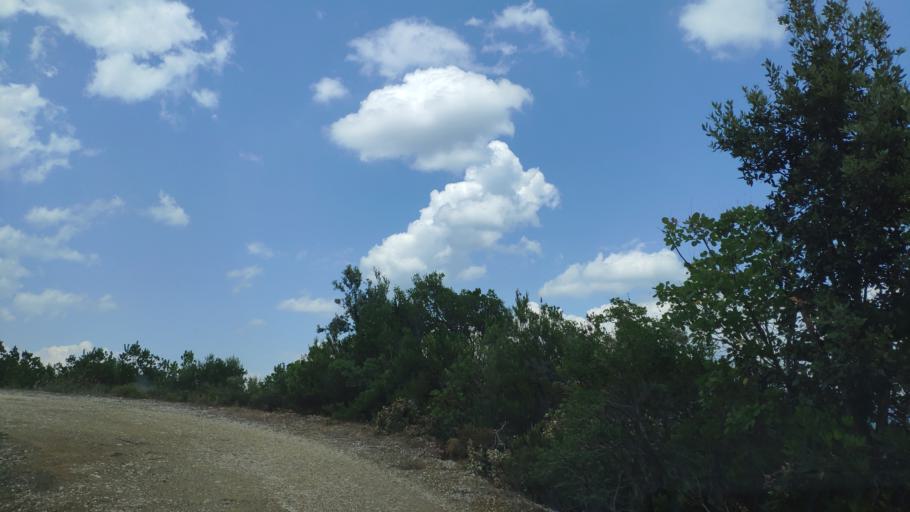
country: GR
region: Epirus
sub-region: Nomos Artas
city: Agios Dimitrios
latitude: 39.3139
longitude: 21.0186
